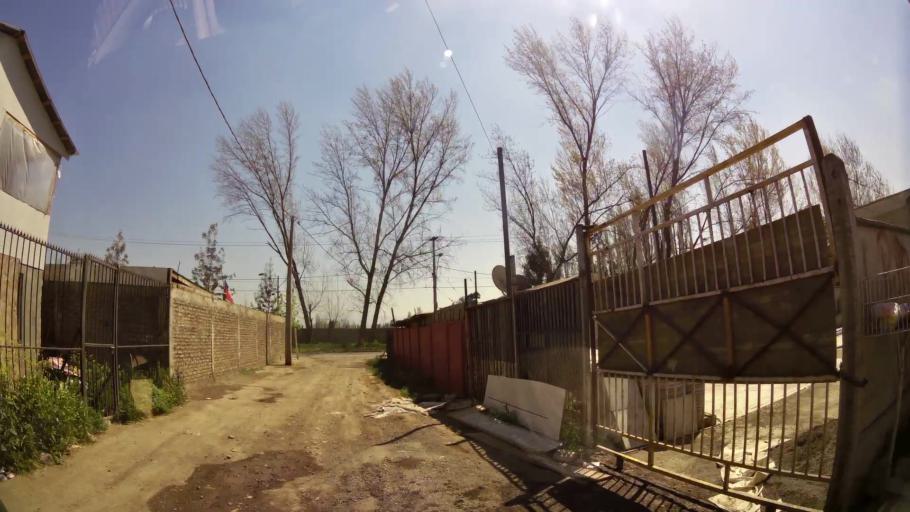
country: CL
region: Santiago Metropolitan
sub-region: Provincia de Talagante
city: Penaflor
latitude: -33.5910
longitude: -70.8112
